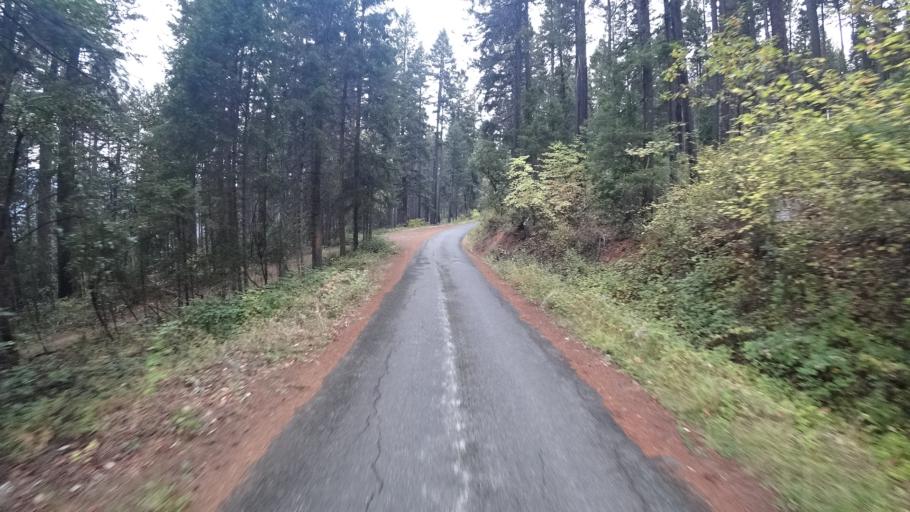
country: US
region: California
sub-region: Siskiyou County
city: Happy Camp
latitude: 41.8005
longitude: -123.3394
